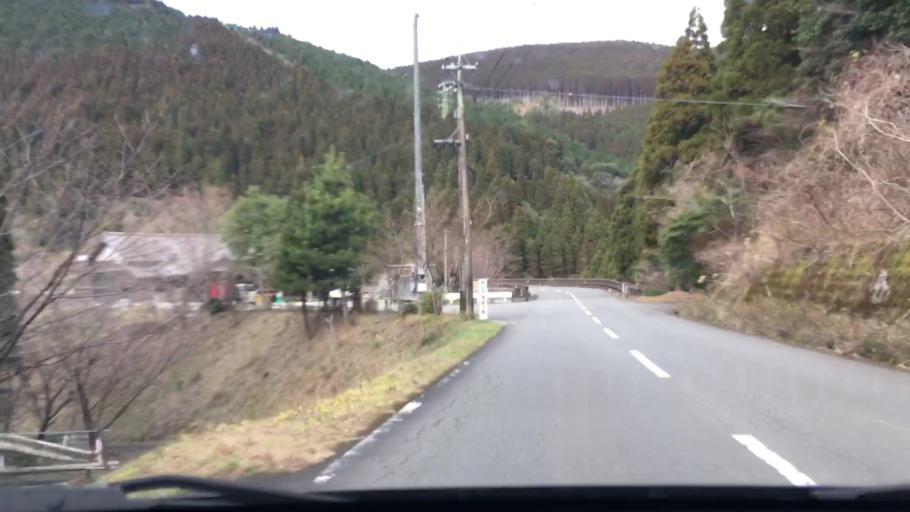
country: JP
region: Miyazaki
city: Nichinan
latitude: 31.6615
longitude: 131.3246
